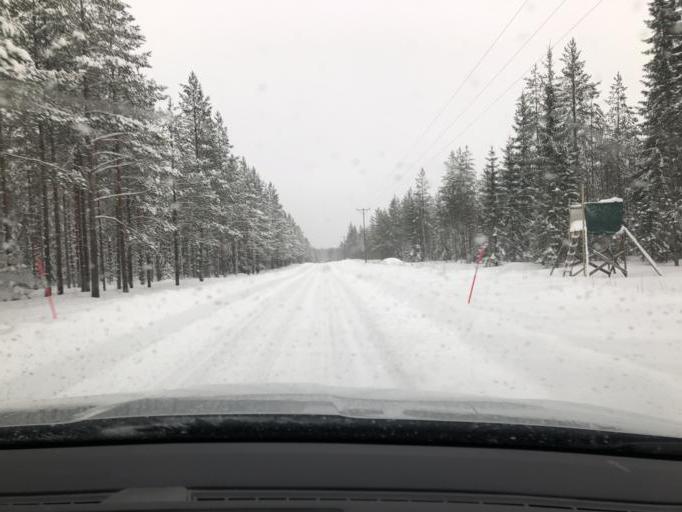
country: SE
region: Vaesterbotten
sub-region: Umea Kommun
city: Saevar
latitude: 63.9465
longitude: 20.6979
